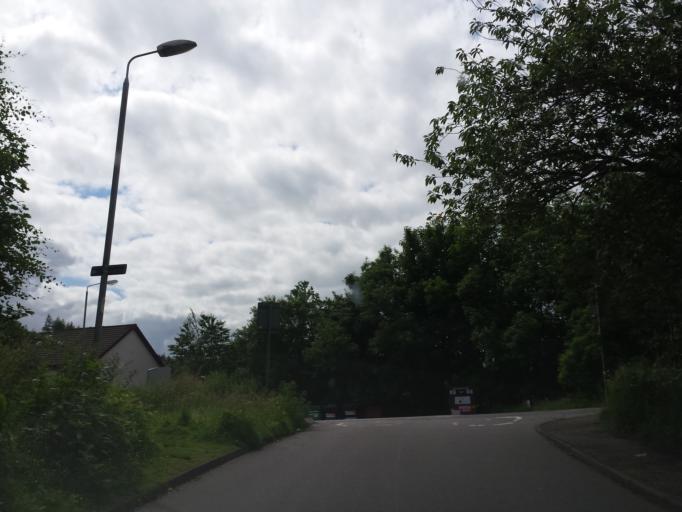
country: GB
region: Scotland
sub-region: Argyll and Bute
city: Oban
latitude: 56.4457
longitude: -5.4420
